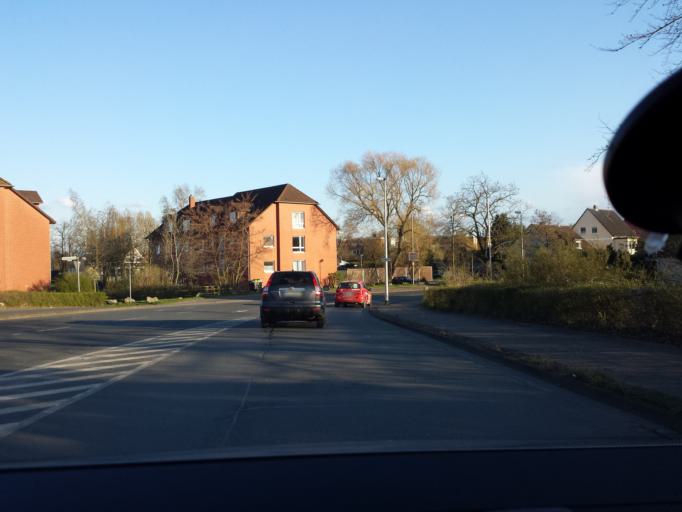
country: DE
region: Lower Saxony
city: Braunschweig
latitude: 52.3102
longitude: 10.4943
